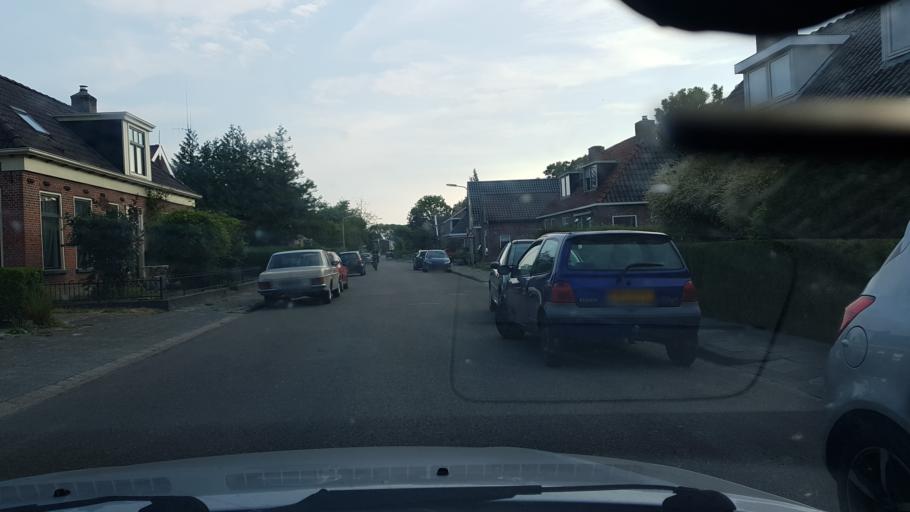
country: NL
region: Friesland
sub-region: Gemeente Ferwerderadiel
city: Burdaard
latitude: 53.2950
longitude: 5.8784
